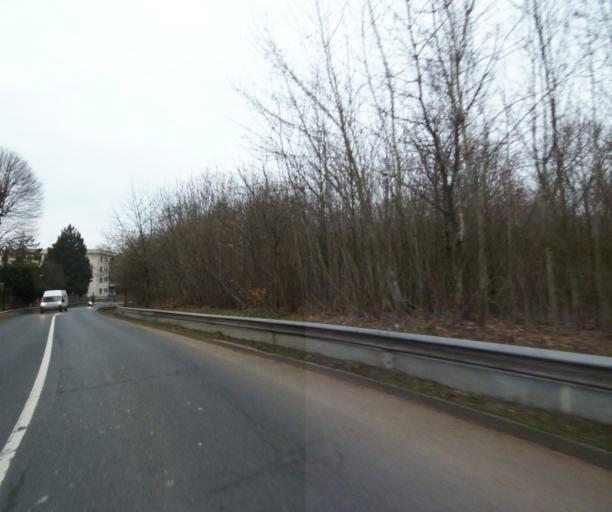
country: FR
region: Ile-de-France
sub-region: Departement des Hauts-de-Seine
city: Vaucresson
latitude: 48.8394
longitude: 2.1457
